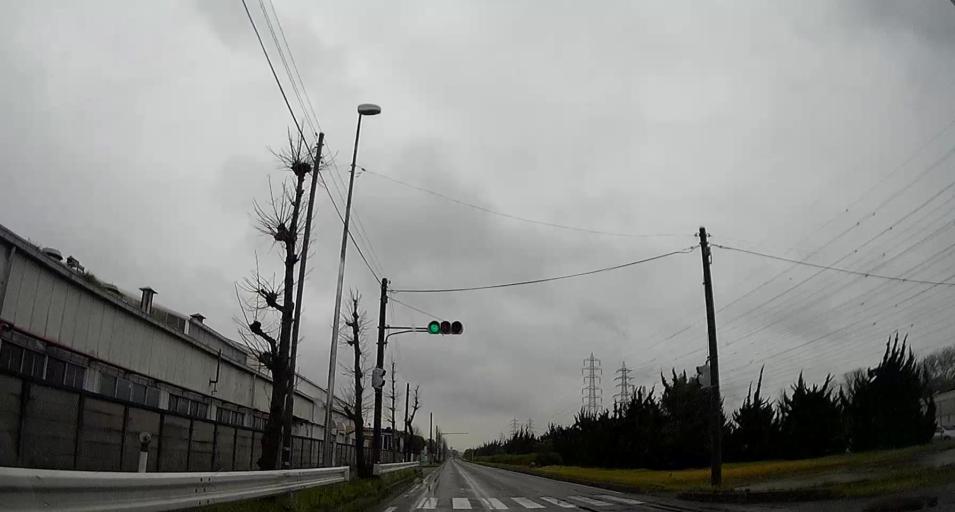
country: JP
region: Chiba
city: Ichihara
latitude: 35.4941
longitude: 140.0454
